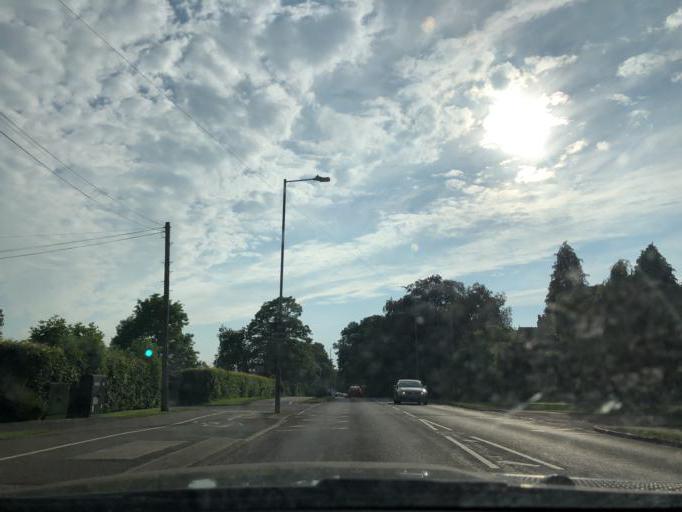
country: GB
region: England
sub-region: Warwickshire
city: Warwick
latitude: 52.2810
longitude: -1.5655
